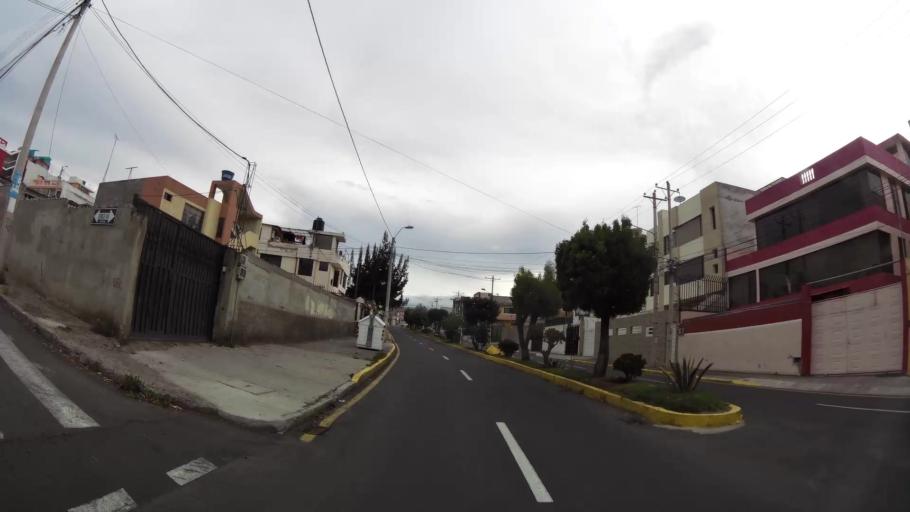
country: EC
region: Tungurahua
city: Ambato
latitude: -1.2615
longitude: -78.6309
